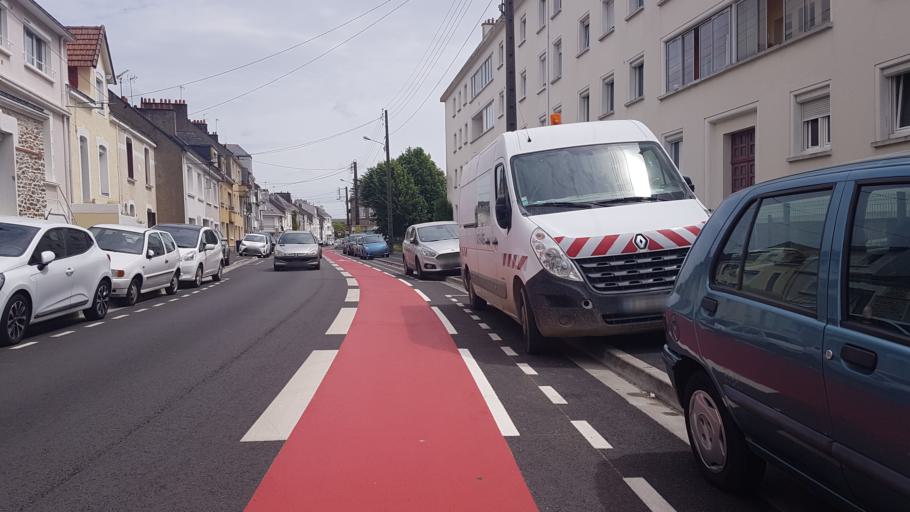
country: FR
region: Pays de la Loire
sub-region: Departement de la Loire-Atlantique
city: Saint-Nazaire
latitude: 47.2781
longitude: -2.2210
